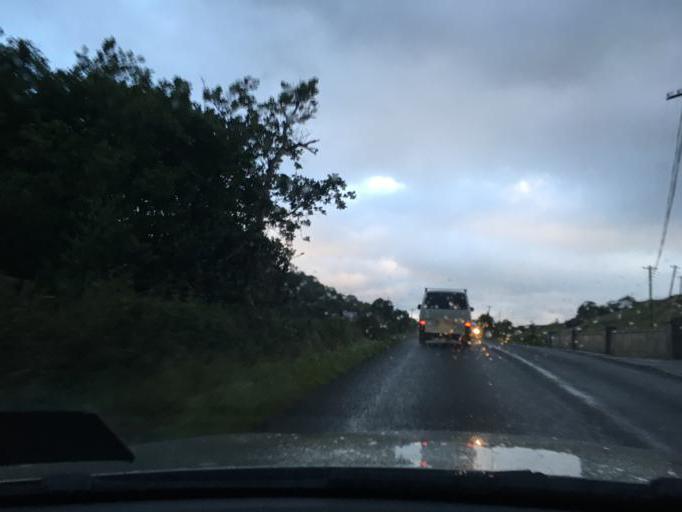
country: IE
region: Ulster
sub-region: County Donegal
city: Killybegs
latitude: 54.6355
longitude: -8.4705
